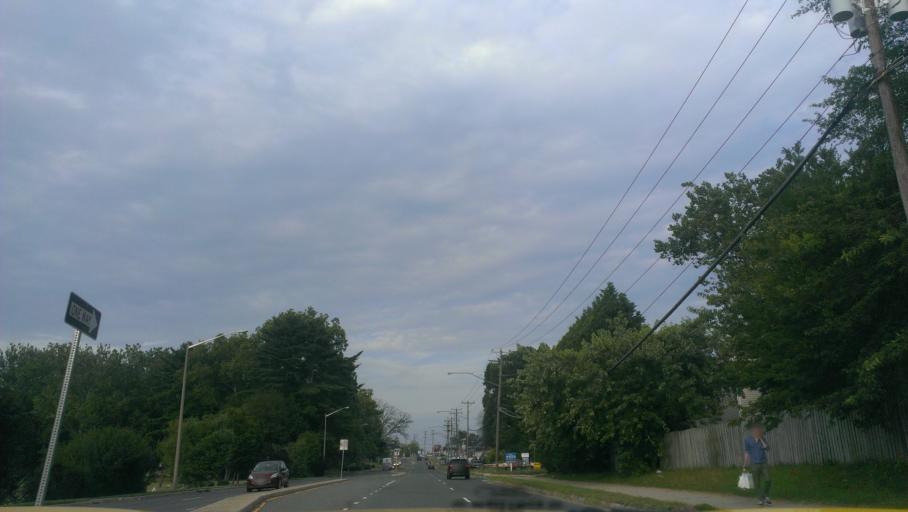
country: US
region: Virginia
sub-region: Fairfax County
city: Jefferson
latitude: 38.8754
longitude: -77.2050
